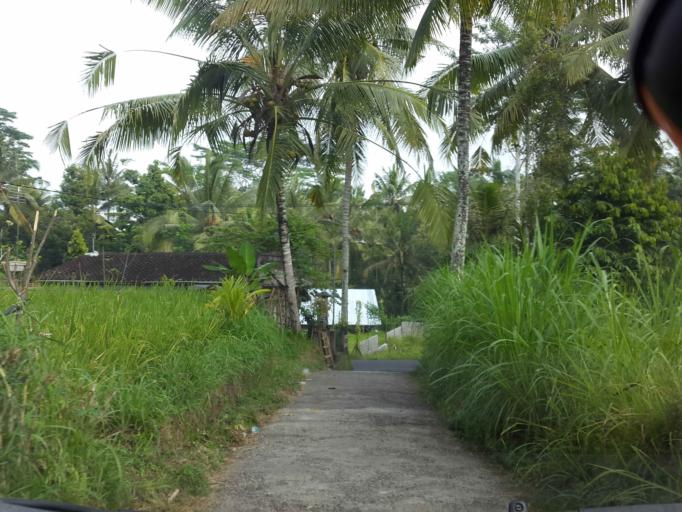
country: ID
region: Bali
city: Banjar Bebalang
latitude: -8.4689
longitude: 115.3818
